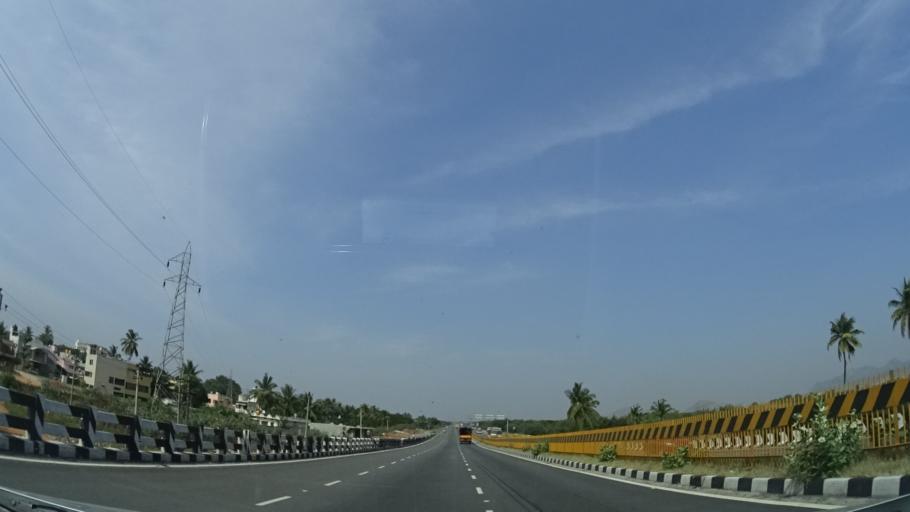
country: IN
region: Karnataka
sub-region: Tumkur
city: Tumkur
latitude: 13.3316
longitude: 77.1303
